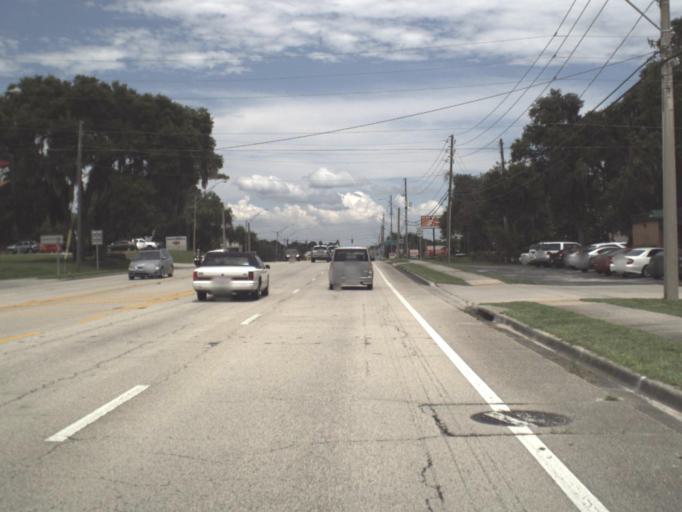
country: US
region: Florida
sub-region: Citrus County
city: Inverness
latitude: 28.8359
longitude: -82.3430
